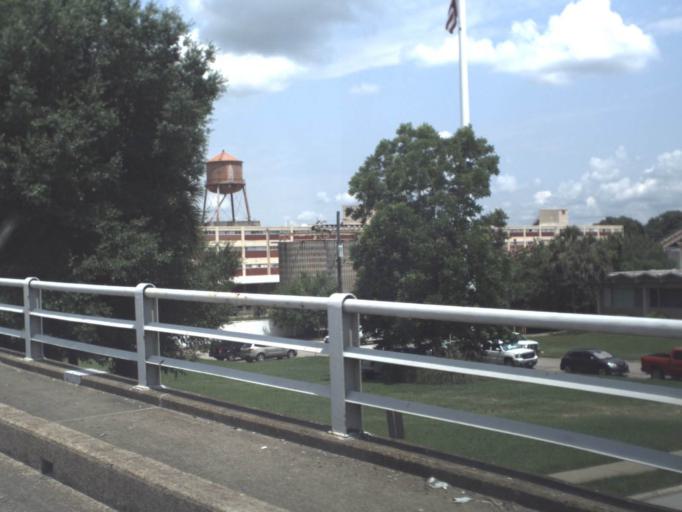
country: US
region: Florida
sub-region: Duval County
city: Jacksonville
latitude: 30.3291
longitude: -81.6456
